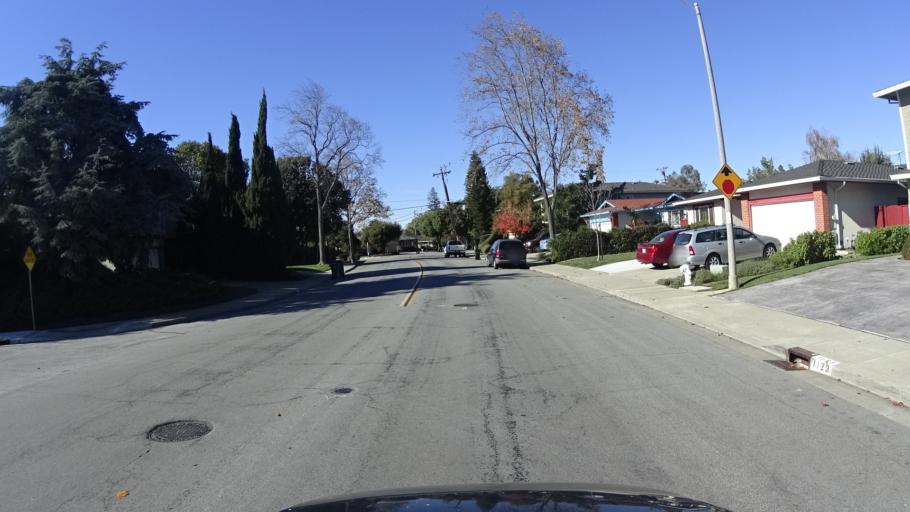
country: US
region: California
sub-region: Santa Clara County
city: Cupertino
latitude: 37.3405
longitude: -122.0015
